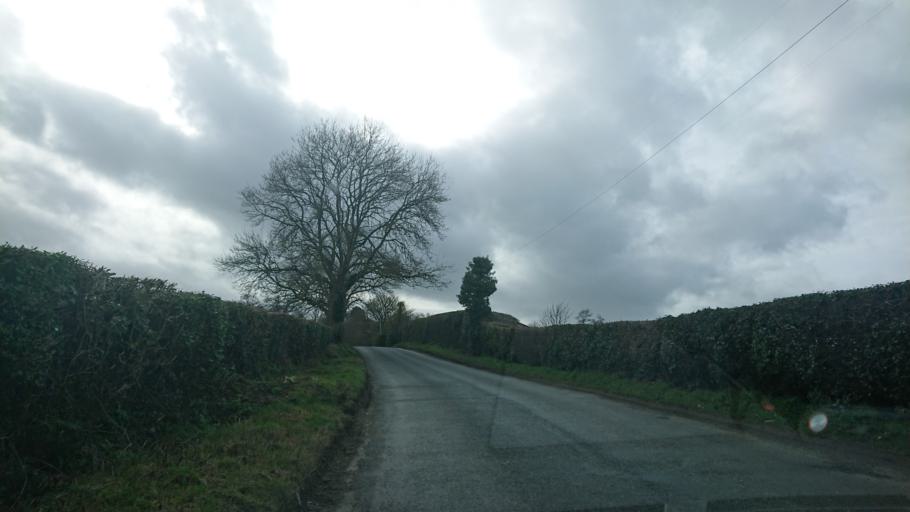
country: IE
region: Leinster
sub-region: Kildare
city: Naas
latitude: 53.1825
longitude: -6.6603
